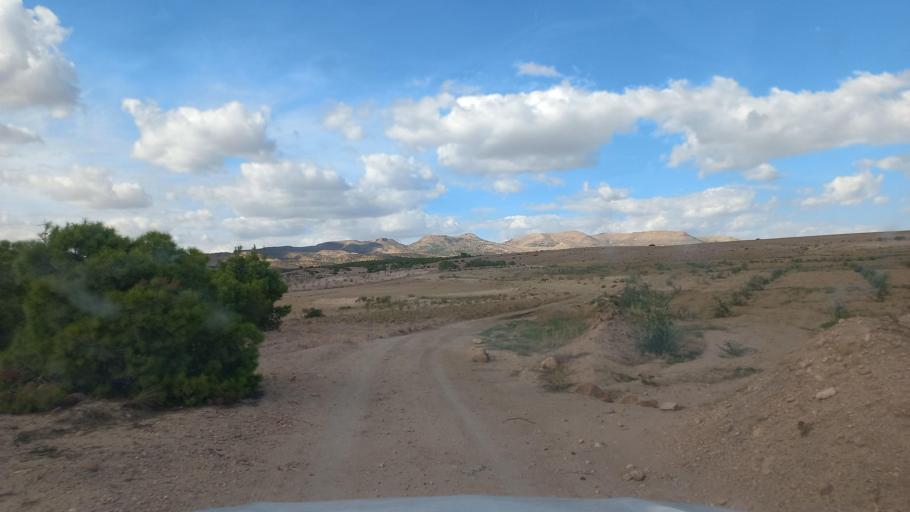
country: TN
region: Al Qasrayn
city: Sbiba
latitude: 35.4004
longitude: 9.0110
